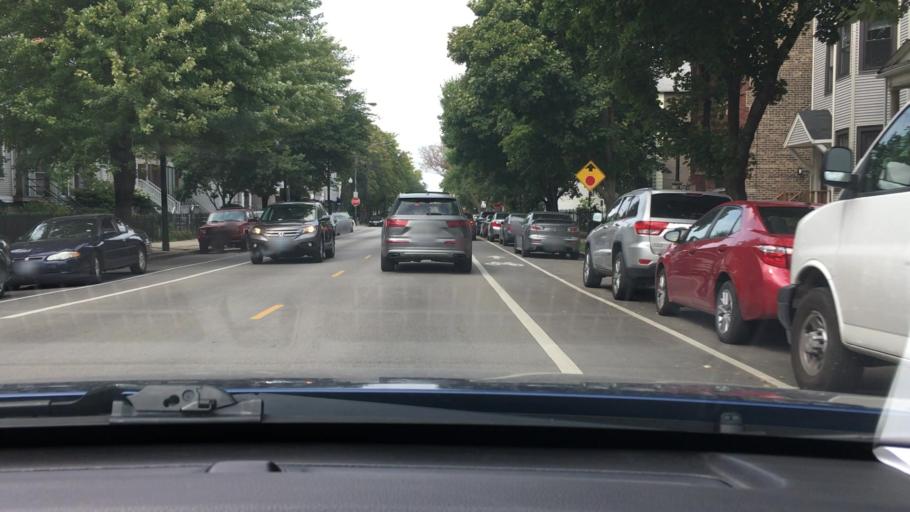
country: US
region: Illinois
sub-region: Cook County
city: Chicago
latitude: 41.9408
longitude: -87.6638
